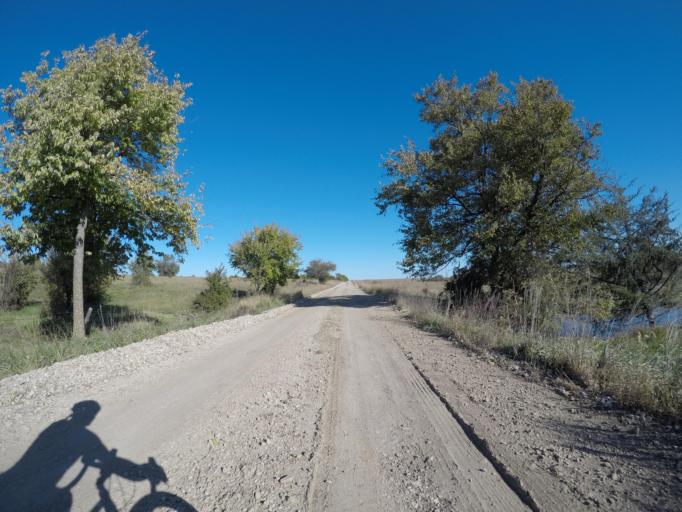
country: US
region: Kansas
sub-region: Wabaunsee County
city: Alma
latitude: 38.8716
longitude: -96.4098
